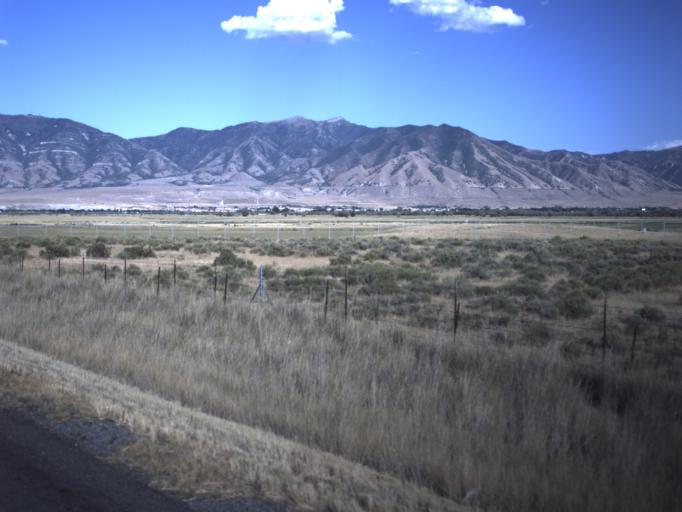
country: US
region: Utah
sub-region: Tooele County
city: Erda
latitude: 40.6242
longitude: -112.3518
